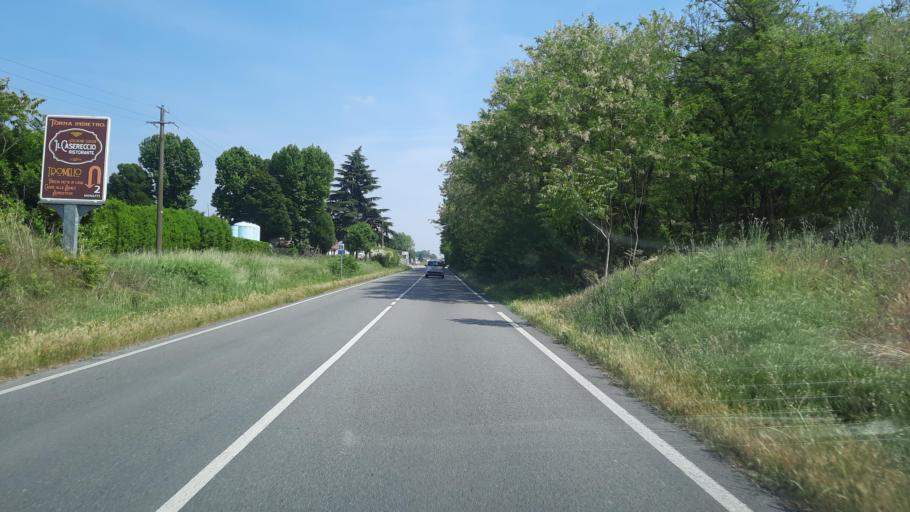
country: IT
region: Lombardy
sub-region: Provincia di Pavia
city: Garlasco
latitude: 45.2028
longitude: 8.8977
